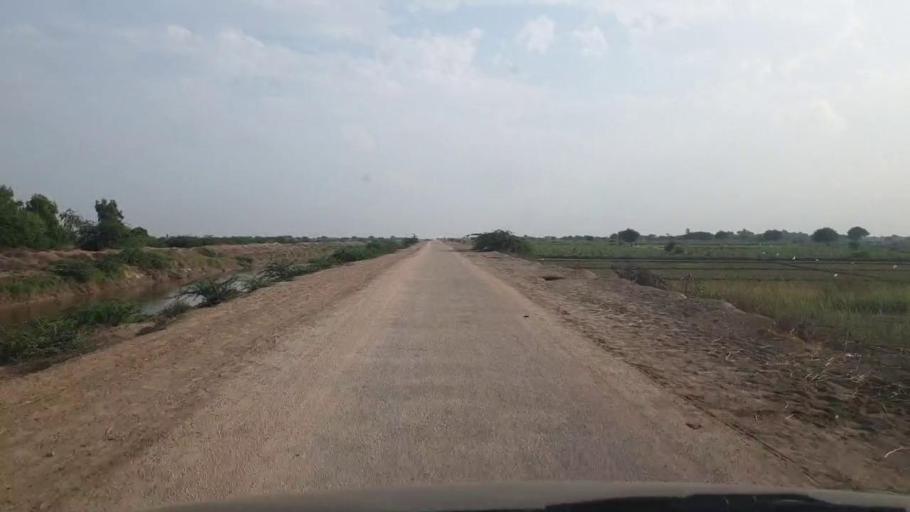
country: PK
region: Sindh
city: Badin
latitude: 24.5459
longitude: 68.6721
